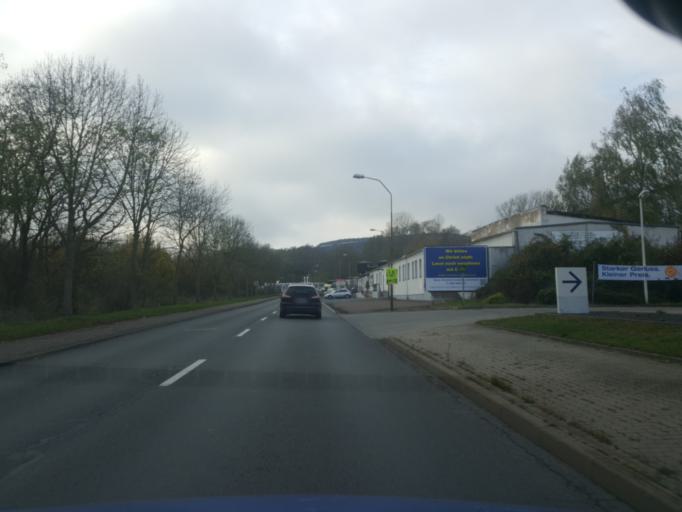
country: DE
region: Saxony-Anhalt
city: Wimmelburg
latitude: 51.5244
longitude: 11.5278
